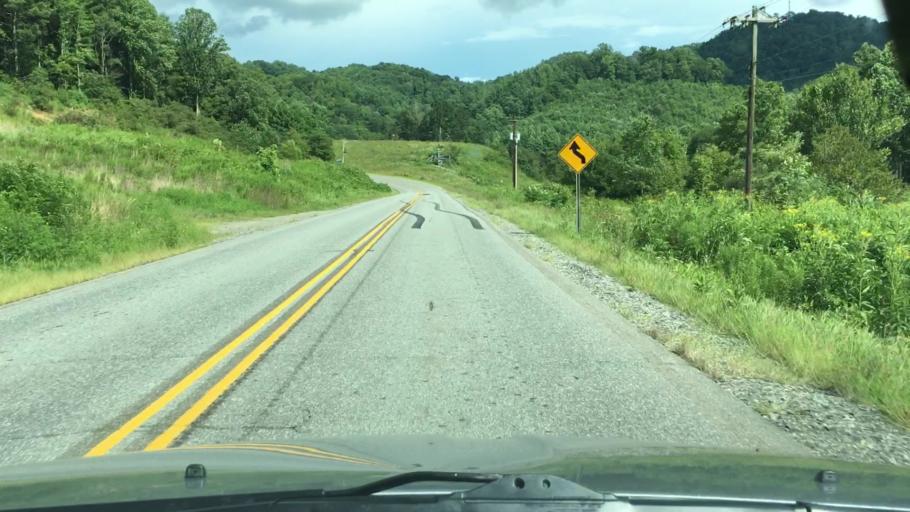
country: US
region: North Carolina
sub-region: Madison County
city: Mars Hill
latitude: 35.9077
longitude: -82.5516
